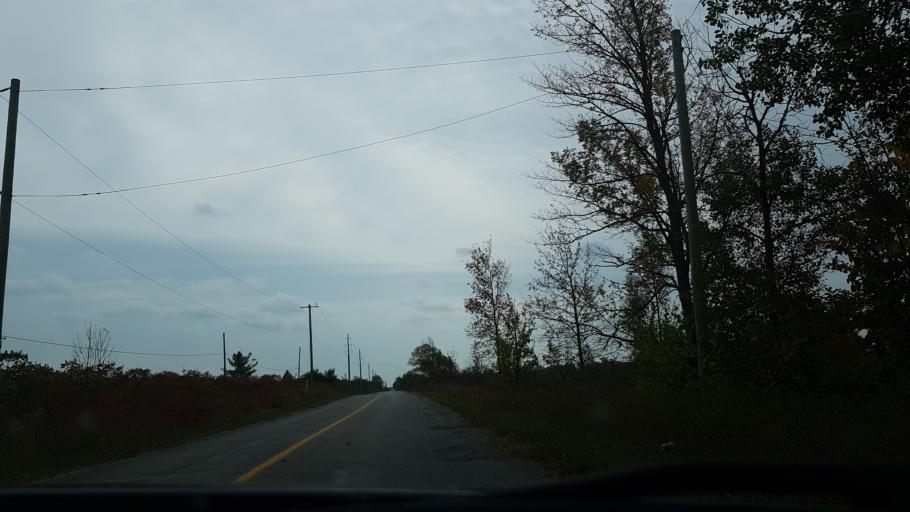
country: CA
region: Ontario
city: Gravenhurst
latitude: 44.6973
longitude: -78.9872
